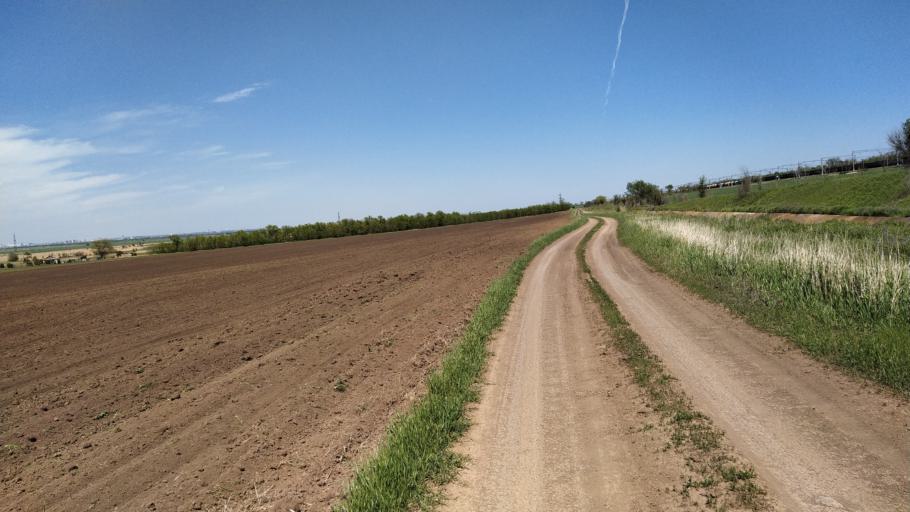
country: RU
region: Rostov
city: Kuleshovka
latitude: 47.0306
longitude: 39.6334
